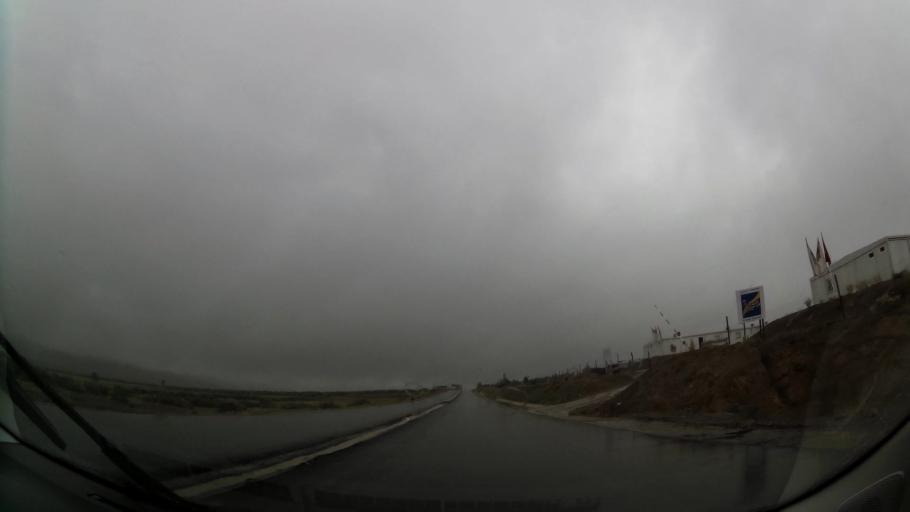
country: MA
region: Oriental
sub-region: Nador
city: Midar
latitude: 34.8644
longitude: -3.7241
